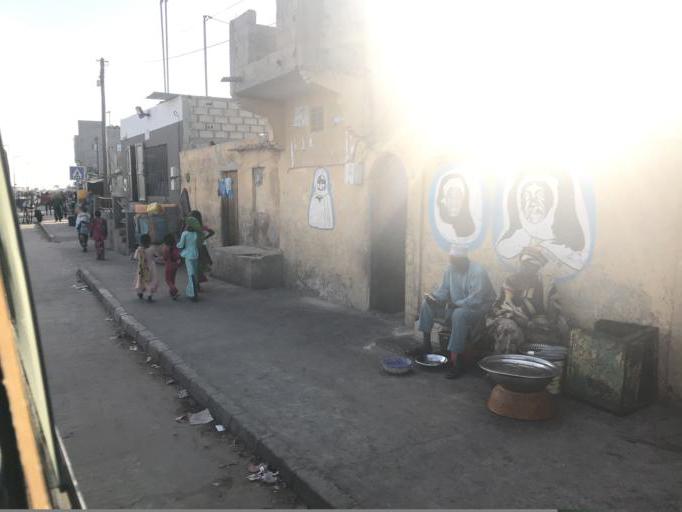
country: SN
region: Saint-Louis
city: Saint-Louis
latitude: 16.0235
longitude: -16.5073
